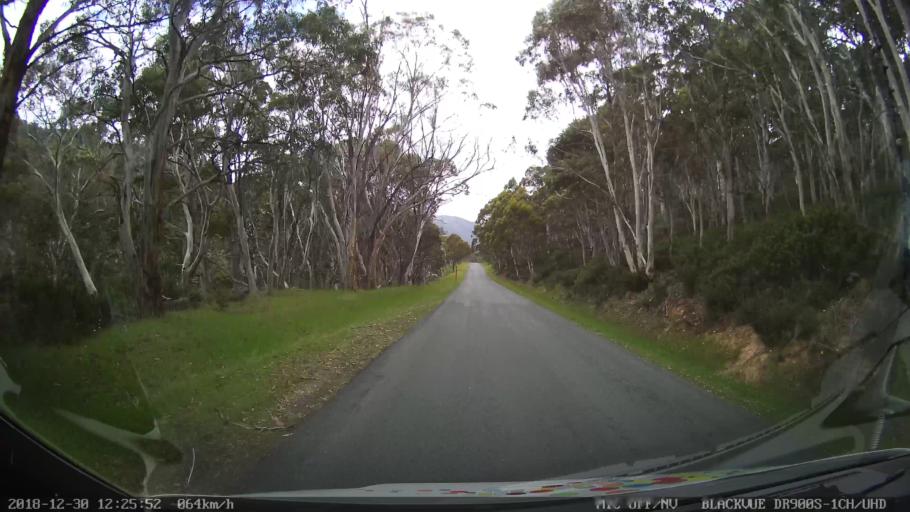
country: AU
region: New South Wales
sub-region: Snowy River
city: Jindabyne
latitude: -36.3454
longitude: 148.4887
